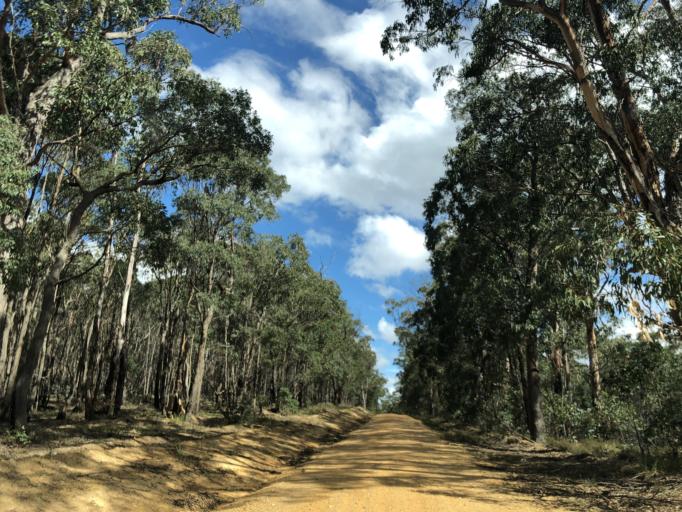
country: AU
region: Victoria
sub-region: Moorabool
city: Bacchus Marsh
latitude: -37.5218
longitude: 144.3225
